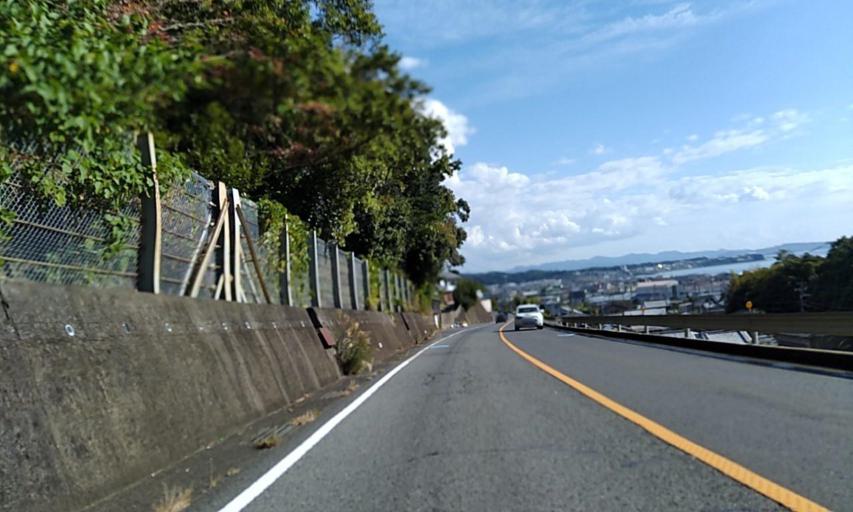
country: JP
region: Wakayama
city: Tanabe
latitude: 33.7784
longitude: 135.3076
